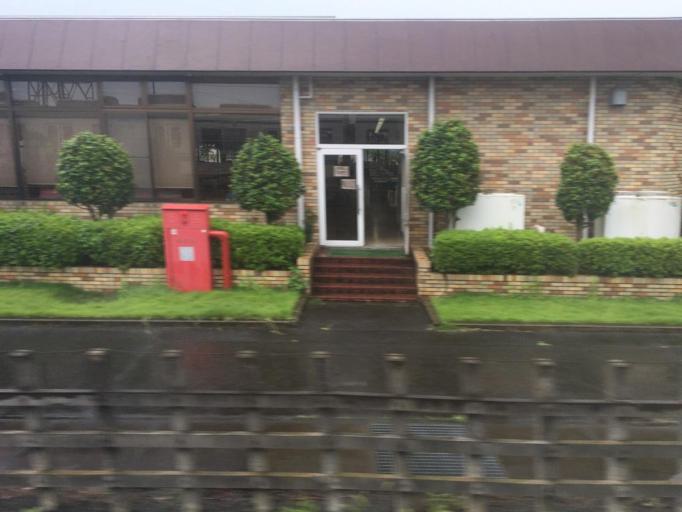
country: JP
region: Gunma
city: Ota
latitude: 36.2860
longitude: 139.3536
